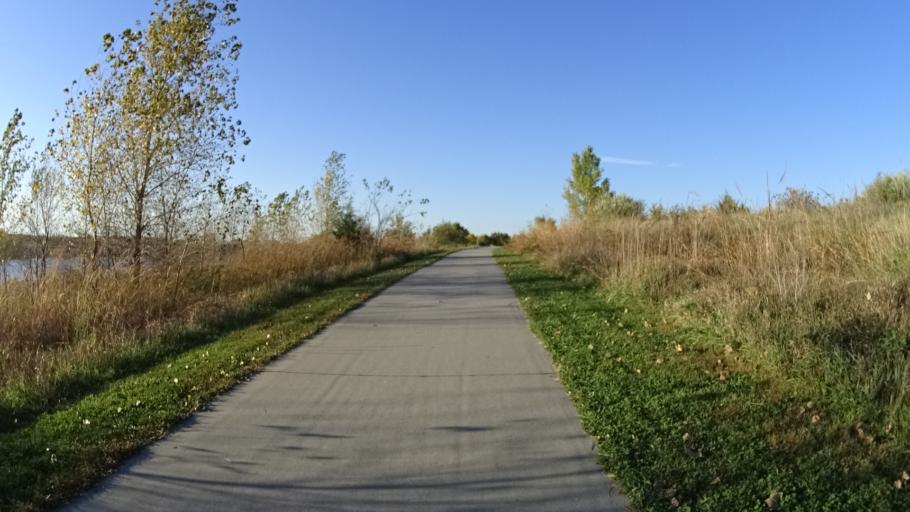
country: US
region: Nebraska
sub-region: Sarpy County
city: Papillion
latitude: 41.1380
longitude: -96.0648
